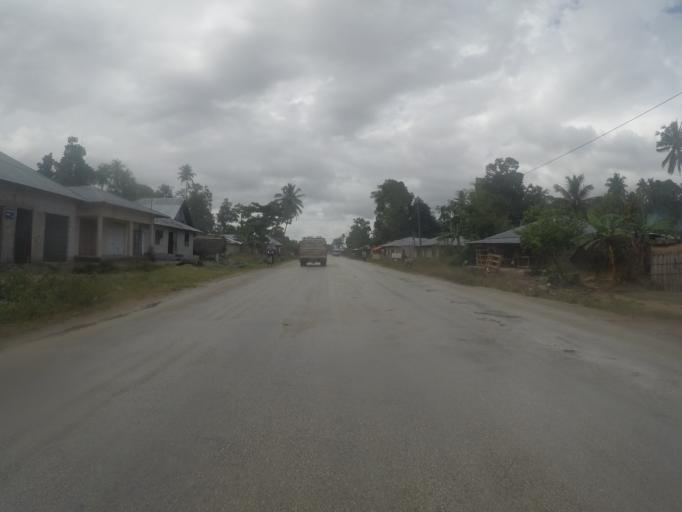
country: TZ
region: Zanzibar Central/South
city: Koani
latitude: -6.0206
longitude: 39.2422
